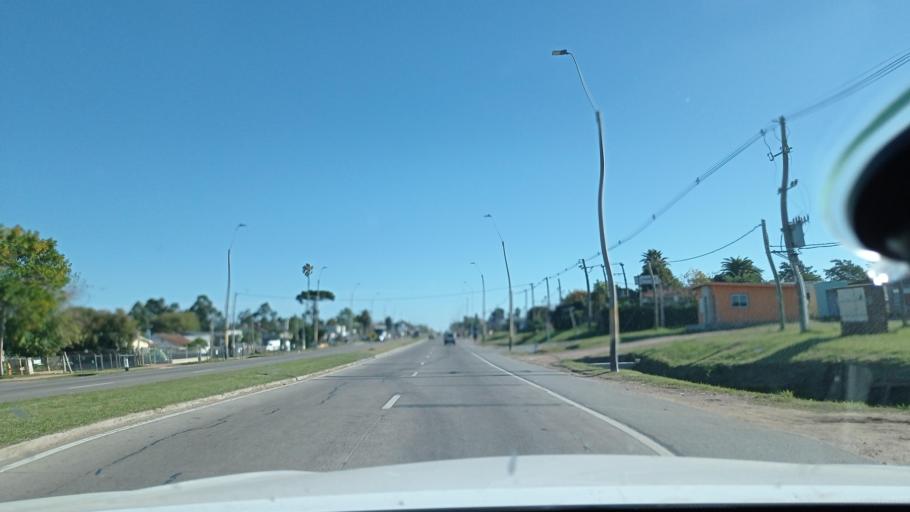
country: UY
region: Canelones
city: Joaquin Suarez
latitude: -34.7575
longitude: -56.0087
